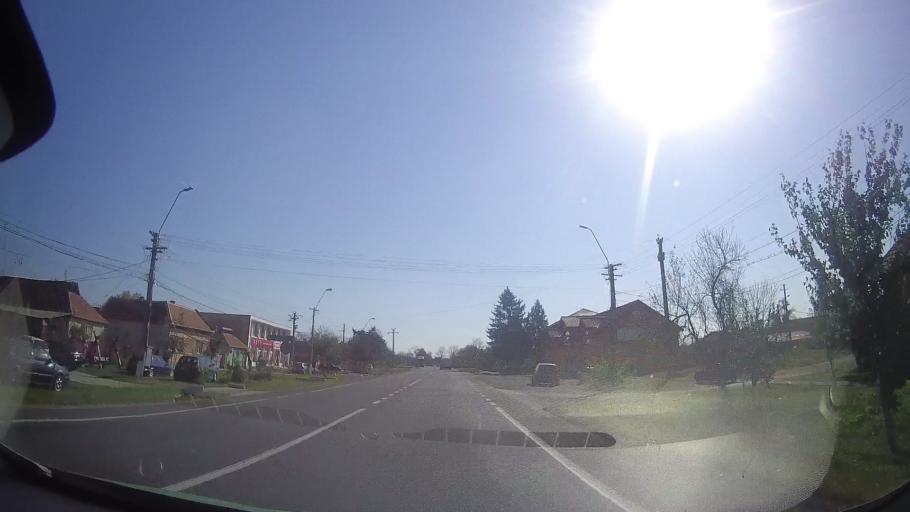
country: RO
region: Timis
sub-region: Comuna Belint
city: Belint
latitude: 45.7506
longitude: 21.7642
